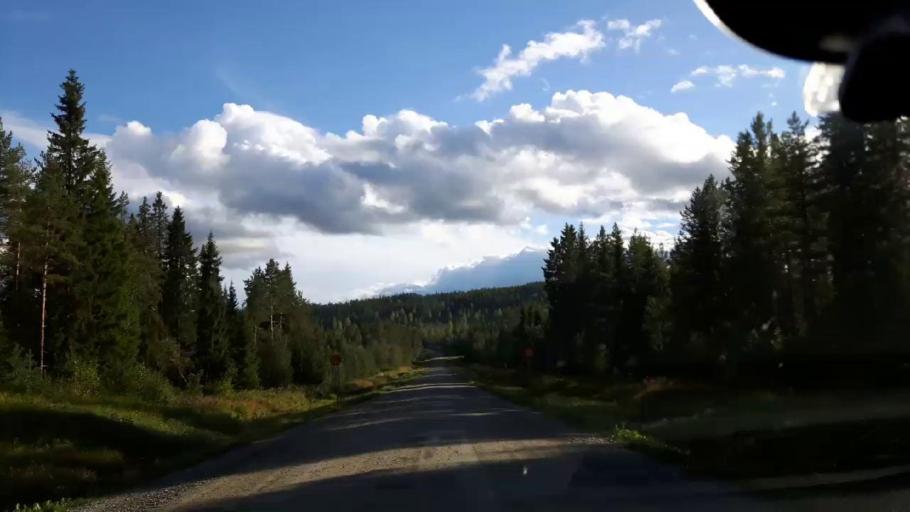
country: SE
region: Jaemtland
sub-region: Stroemsunds Kommun
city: Stroemsund
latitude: 63.3609
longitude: 15.5690
